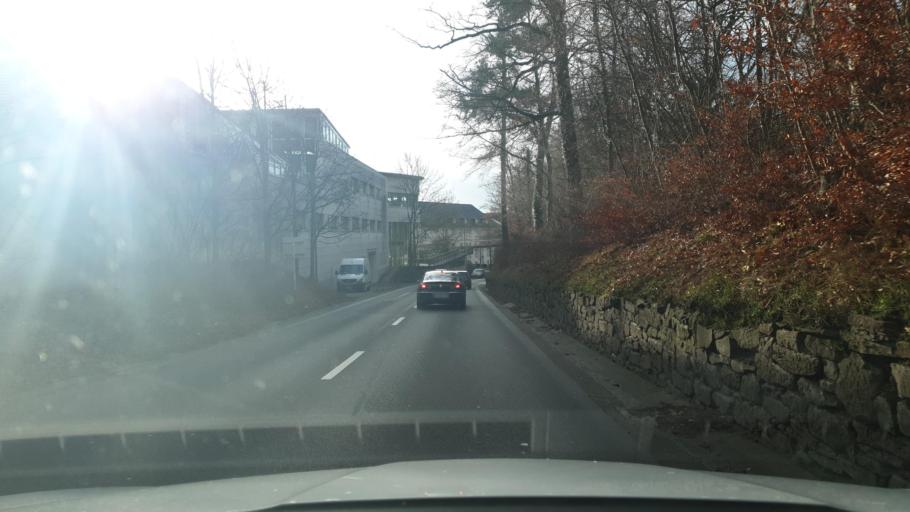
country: DE
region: North Rhine-Westphalia
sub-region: Regierungsbezirk Detmold
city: Bad Salzuflen
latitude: 52.0898
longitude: 8.7470
